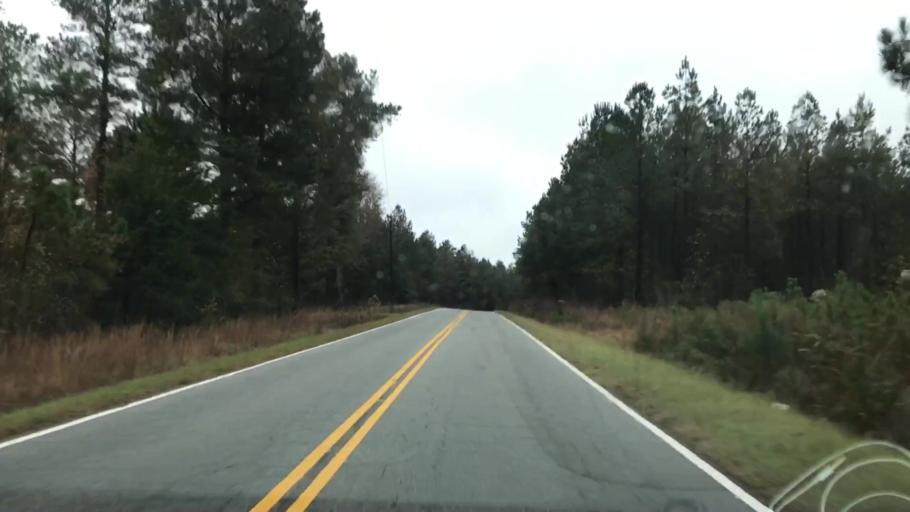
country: US
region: South Carolina
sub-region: Laurens County
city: Joanna
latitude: 34.3700
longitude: -81.7806
